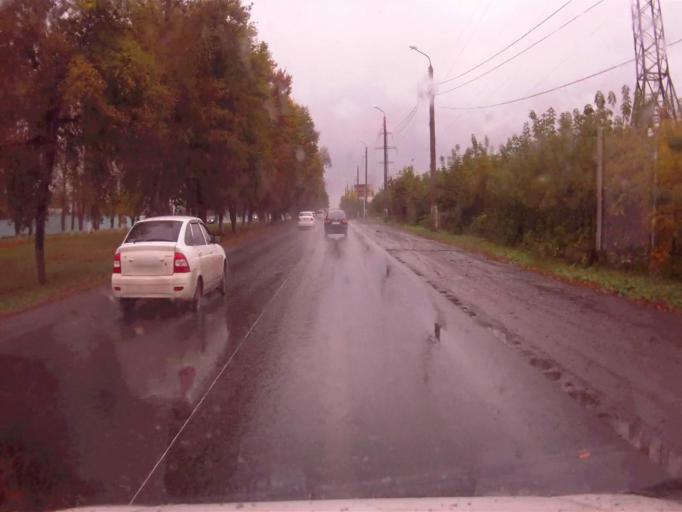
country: RU
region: Chelyabinsk
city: Dolgoderevenskoye
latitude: 55.2495
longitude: 61.3568
